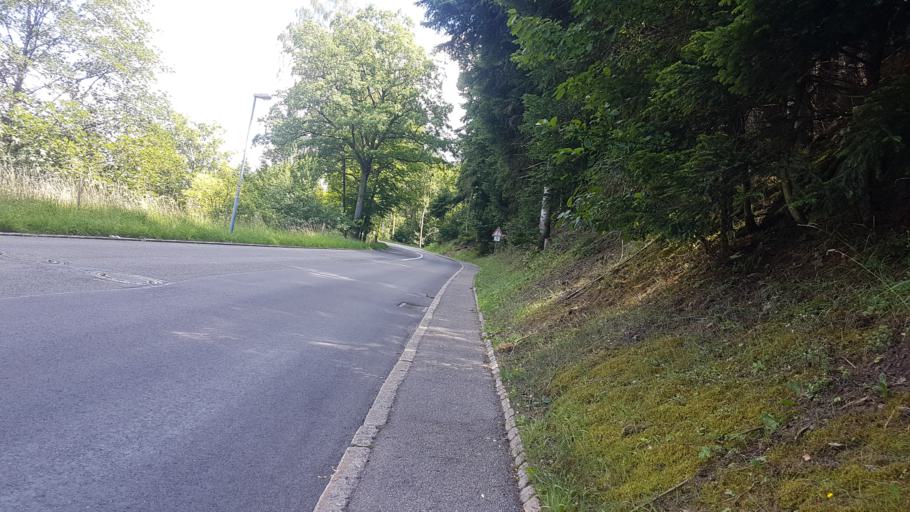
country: DE
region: Baden-Wuerttemberg
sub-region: Freiburg Region
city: Schramberg
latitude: 48.2290
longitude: 8.4000
